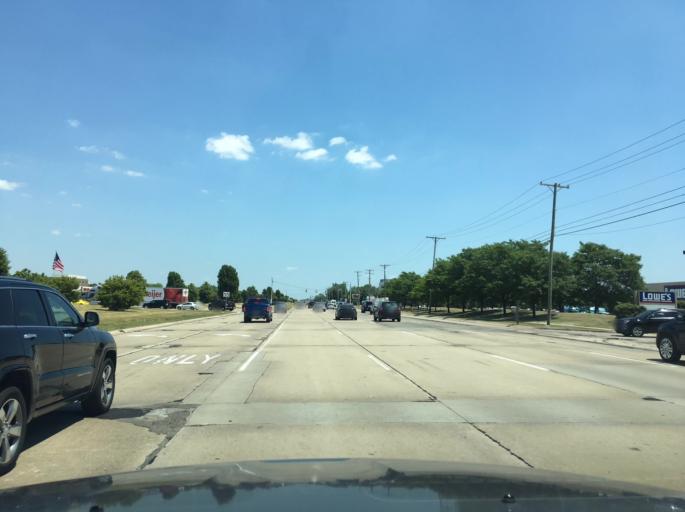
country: US
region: Michigan
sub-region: Macomb County
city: Utica
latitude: 42.6273
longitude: -82.9708
